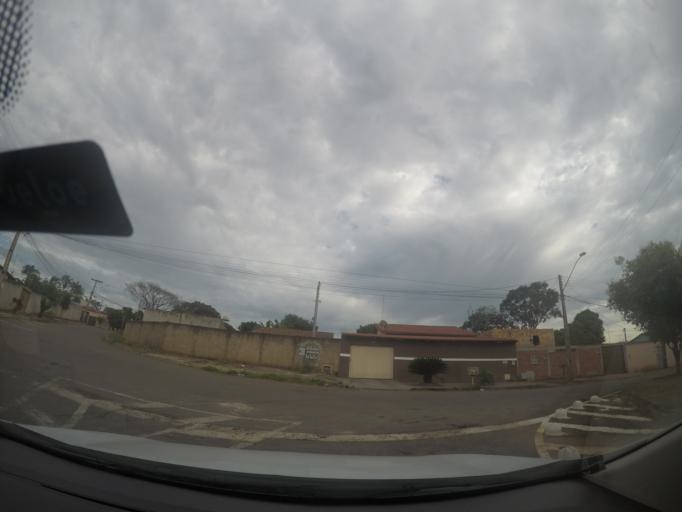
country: BR
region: Goias
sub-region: Goiania
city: Goiania
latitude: -16.6761
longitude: -49.2084
